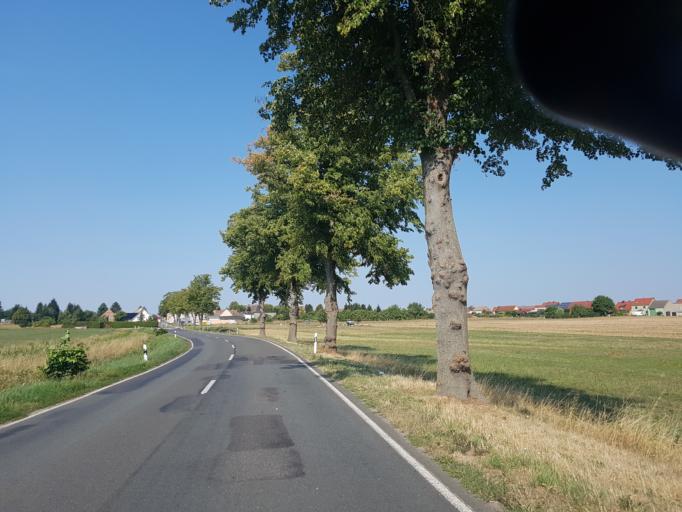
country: DE
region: Brandenburg
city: Gorzke
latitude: 52.1096
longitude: 12.3782
